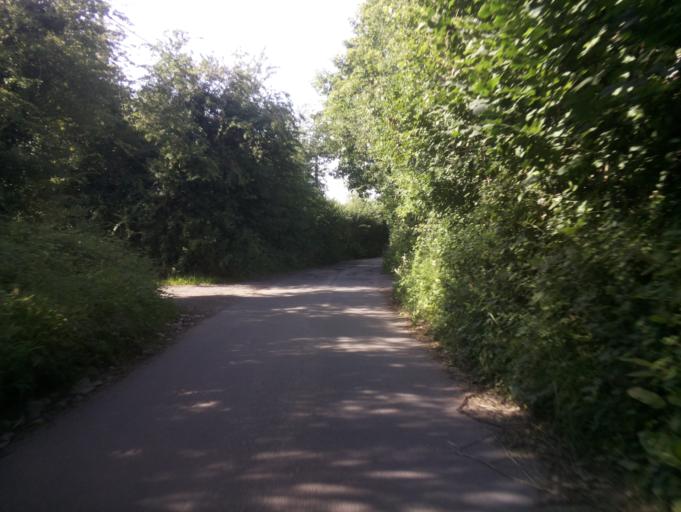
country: GB
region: England
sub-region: South Gloucestershire
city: Bitton
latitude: 51.4391
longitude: -2.4480
